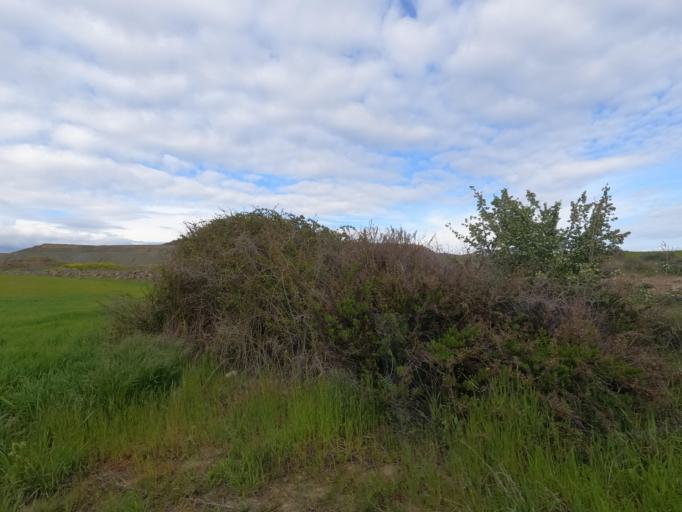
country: CY
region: Lefkosia
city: Lefka
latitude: 35.0948
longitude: 32.9090
